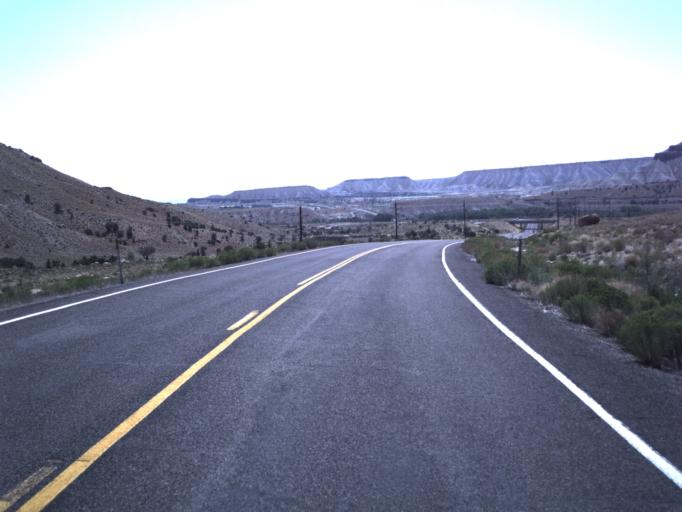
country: US
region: Utah
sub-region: Emery County
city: Orangeville
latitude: 39.2622
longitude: -111.0989
